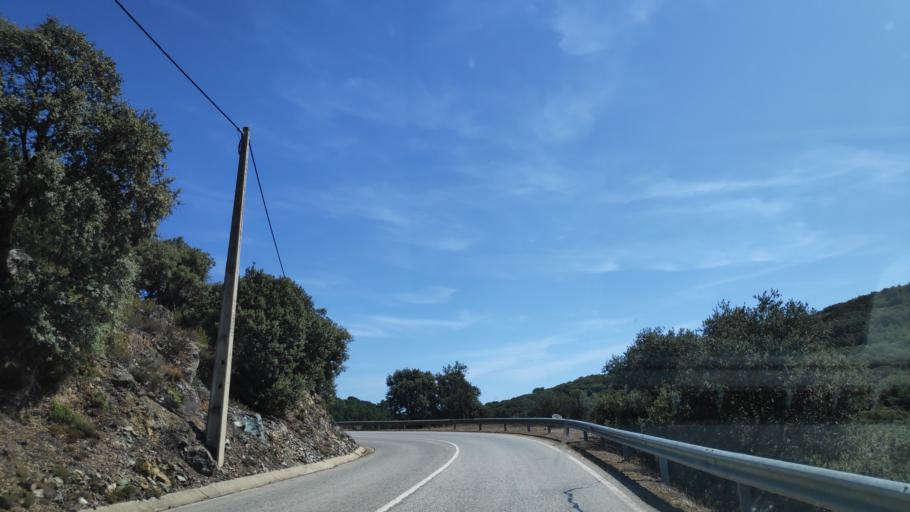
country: PT
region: Braganca
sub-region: Braganca Municipality
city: Braganca
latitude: 41.8351
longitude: -6.7482
